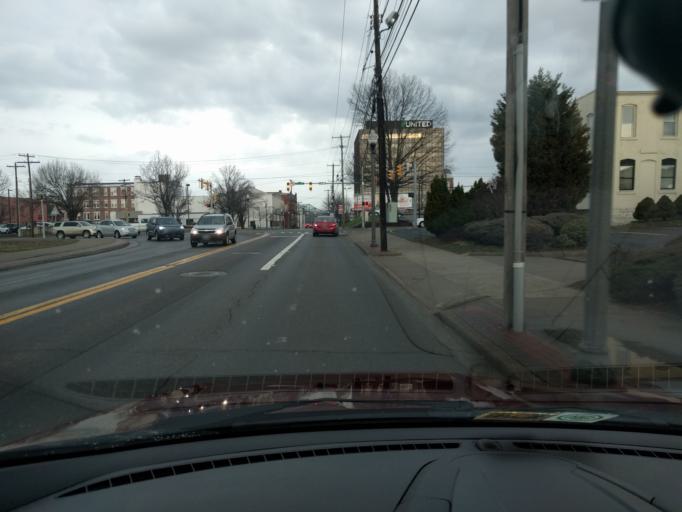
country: US
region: West Virginia
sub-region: Wood County
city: Parkersburg
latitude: 39.2635
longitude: -81.5583
